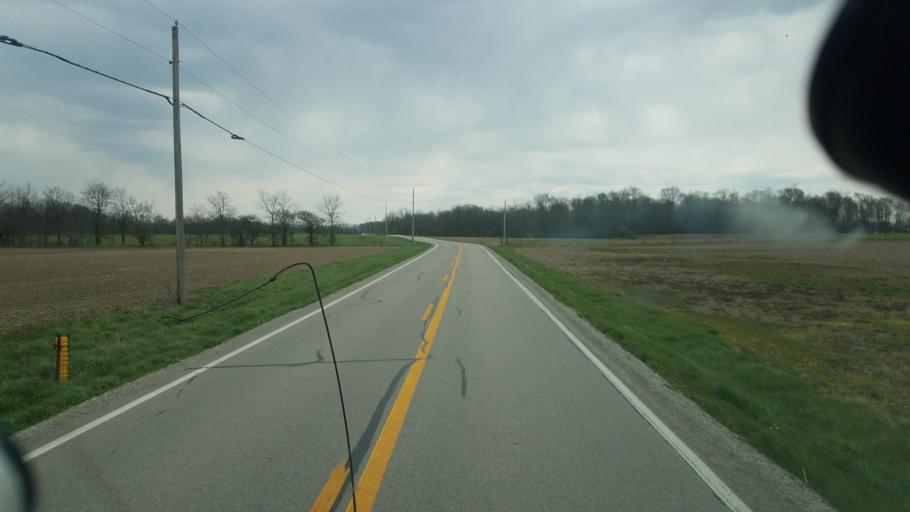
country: US
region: Ohio
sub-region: Marion County
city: Prospect
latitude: 40.4171
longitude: -83.2117
